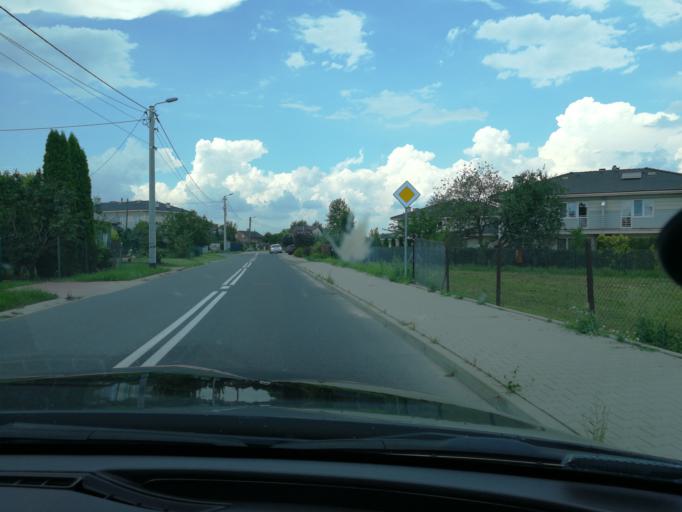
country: PL
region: Lodz Voivodeship
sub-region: Skierniewice
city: Skierniewice
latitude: 51.9736
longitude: 20.1263
